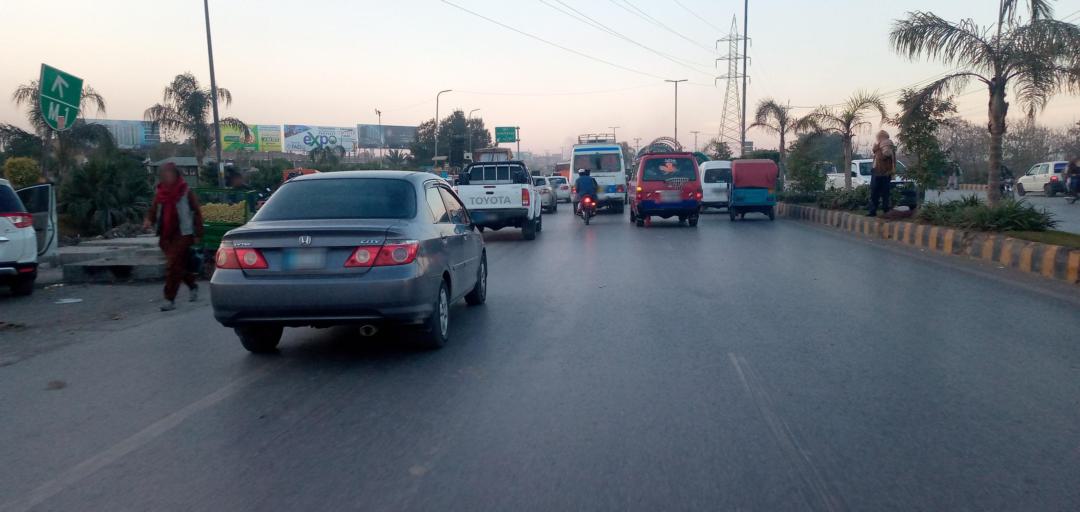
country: PK
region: Khyber Pakhtunkhwa
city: Peshawar
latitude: 34.0256
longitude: 71.6193
